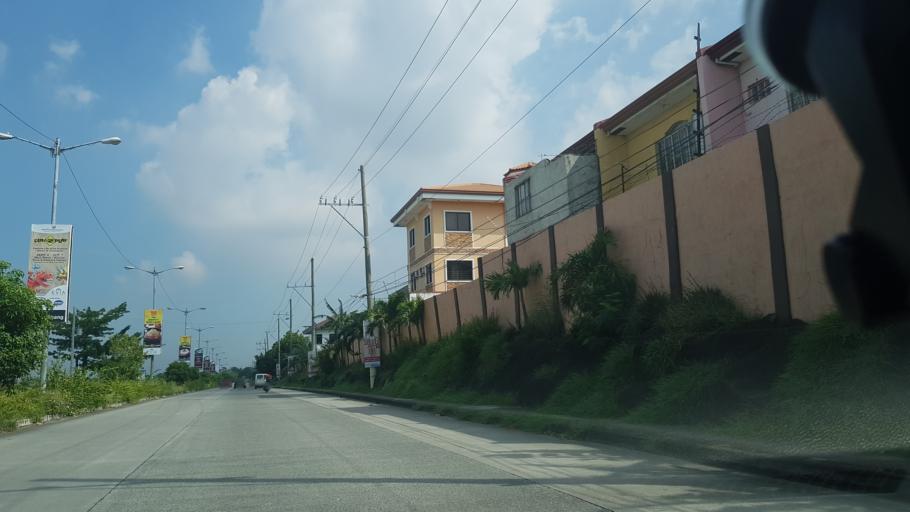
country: PH
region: Calabarzon
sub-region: Province of Laguna
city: San Pedro
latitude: 14.3866
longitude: 121.0101
